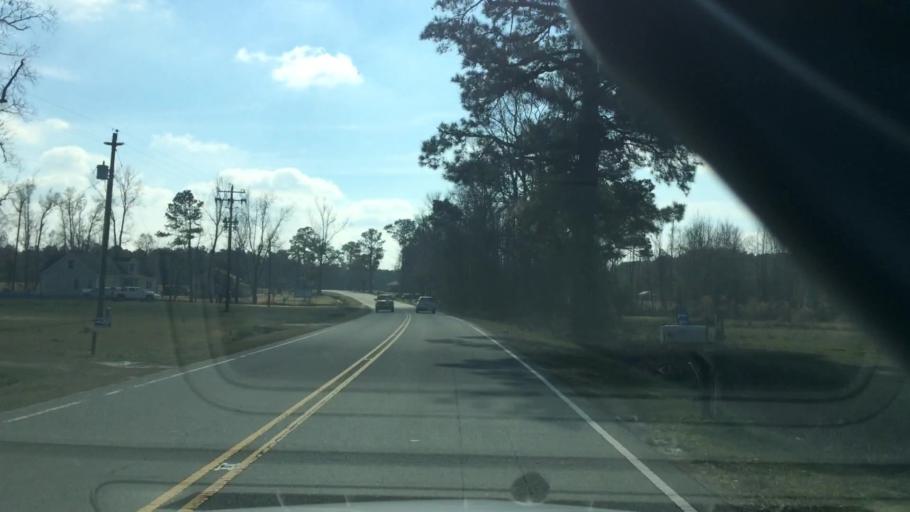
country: US
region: North Carolina
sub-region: Duplin County
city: Beulaville
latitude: 34.8567
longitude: -77.7975
